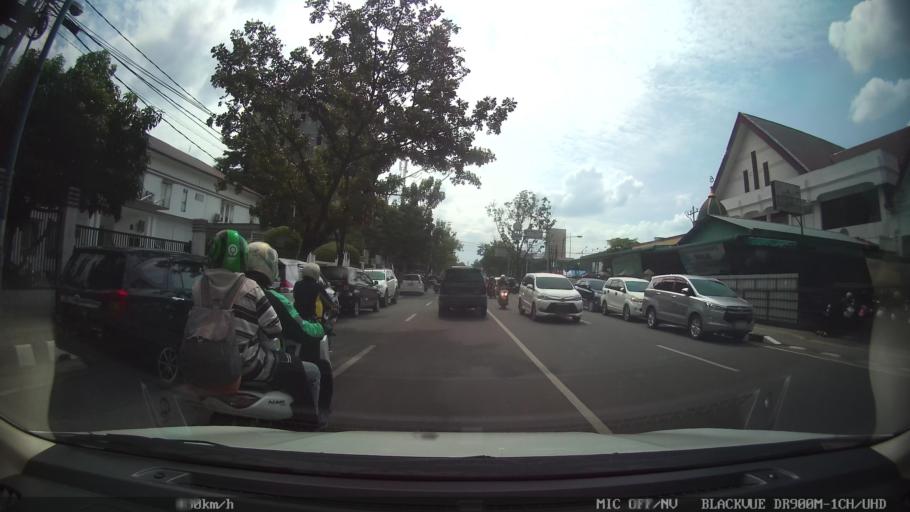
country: ID
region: North Sumatra
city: Medan
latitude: 3.5869
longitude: 98.6726
